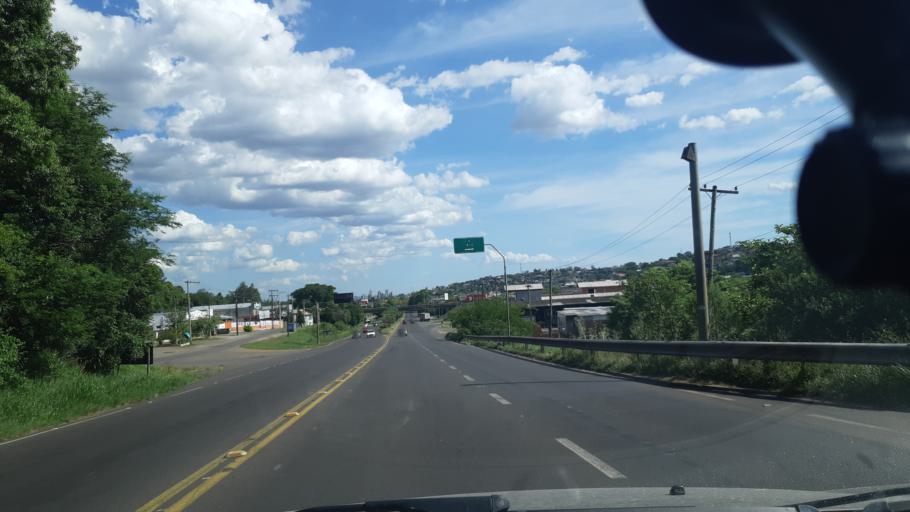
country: BR
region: Rio Grande do Sul
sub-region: Novo Hamburgo
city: Novo Hamburgo
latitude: -29.6536
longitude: -51.1447
